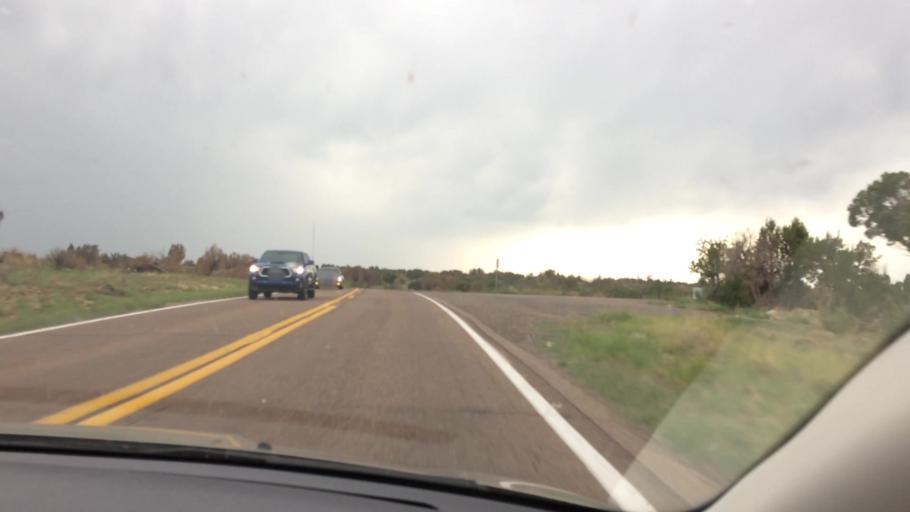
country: US
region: Arizona
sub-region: Navajo County
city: Heber-Overgaard
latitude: 34.5048
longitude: -110.4511
